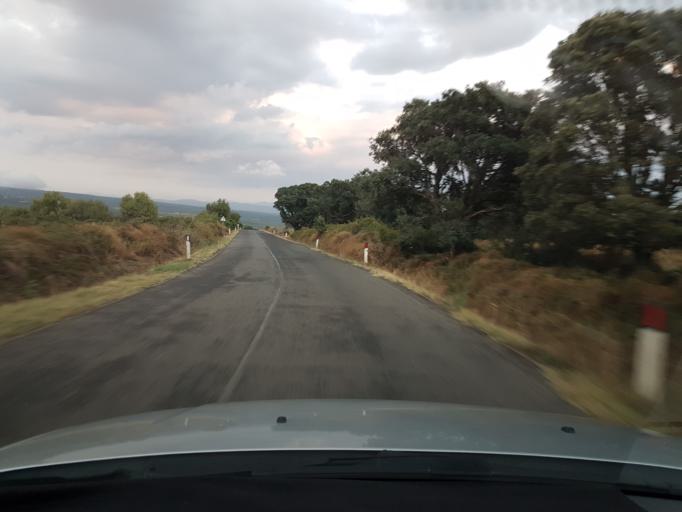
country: IT
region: Sardinia
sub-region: Provincia di Oristano
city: Seneghe
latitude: 40.0688
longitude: 8.6250
